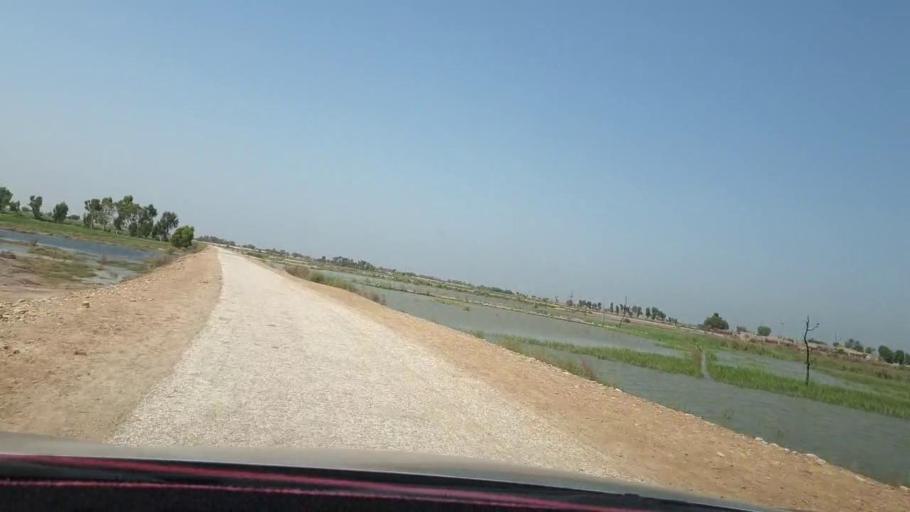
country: PK
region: Sindh
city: Warah
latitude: 27.5441
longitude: 67.7438
